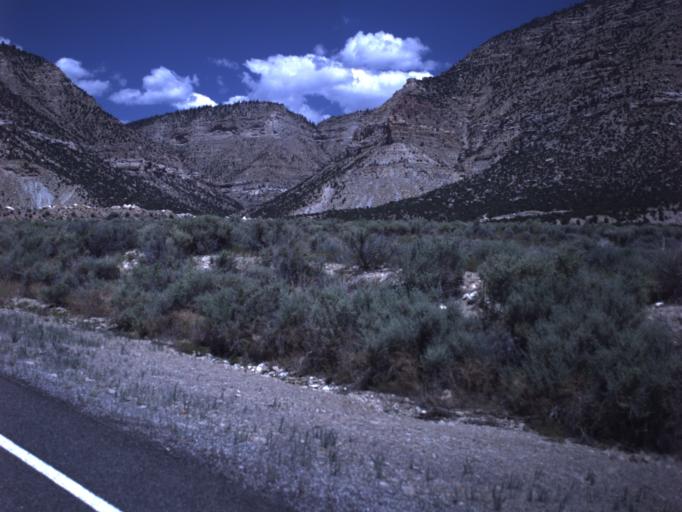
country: US
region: Utah
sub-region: Emery County
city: Orangeville
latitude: 39.2963
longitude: -111.1138
